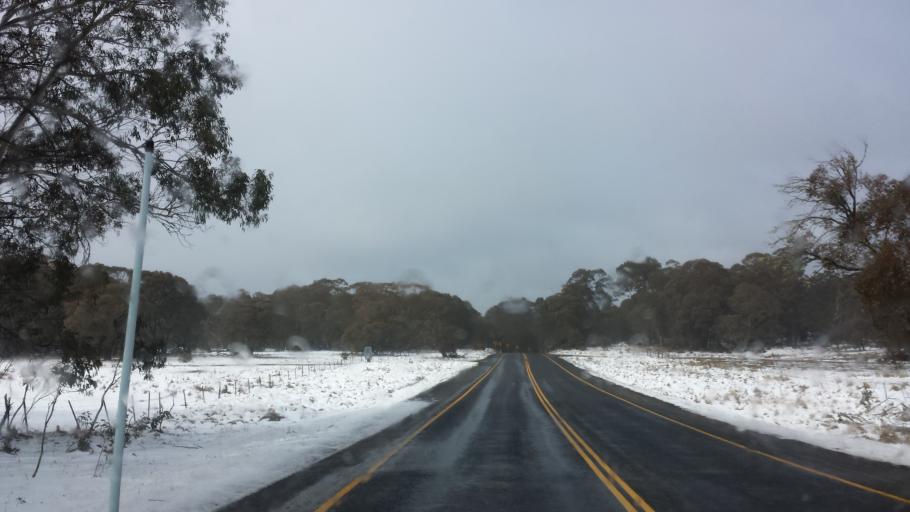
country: AU
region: Victoria
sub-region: Alpine
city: Mount Beauty
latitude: -37.0347
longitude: 147.3030
